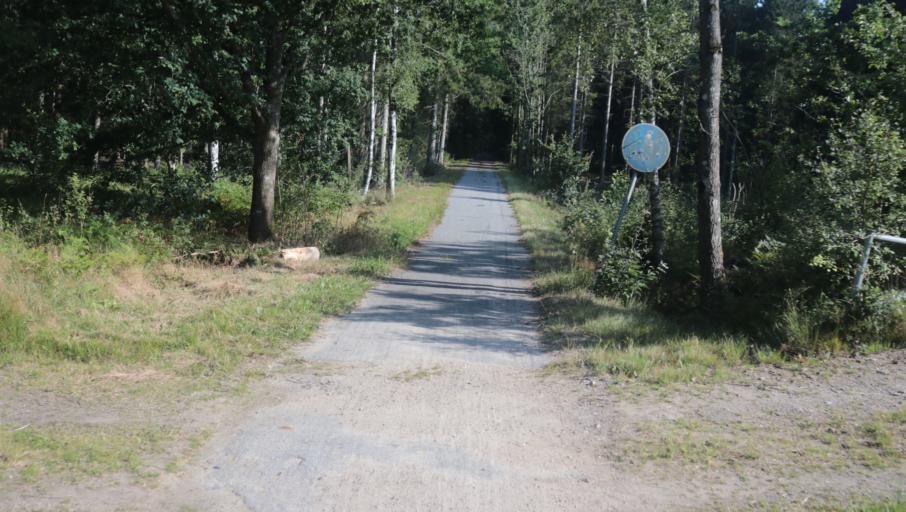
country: SE
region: Blekinge
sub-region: Karlshamns Kommun
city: Svangsta
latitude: 56.3187
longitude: 14.7074
